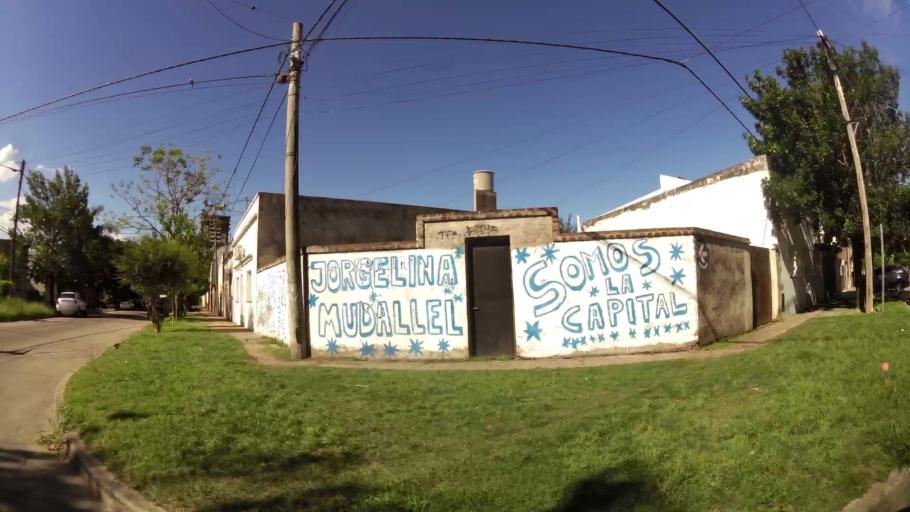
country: AR
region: Santa Fe
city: Santa Fe de la Vera Cruz
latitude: -31.6274
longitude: -60.6959
